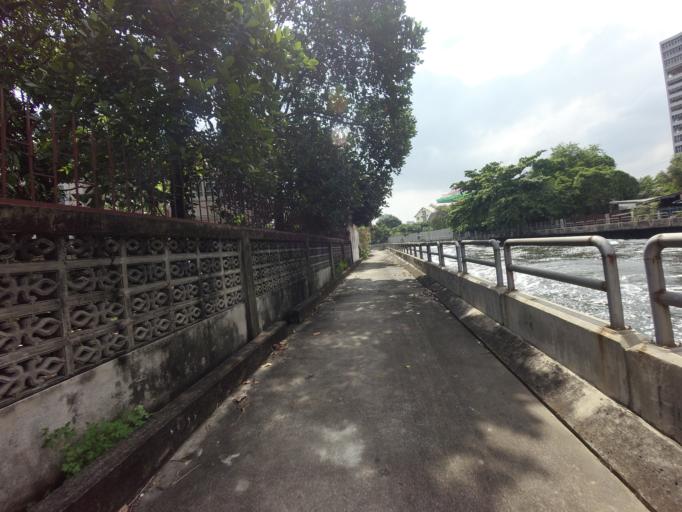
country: TH
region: Bangkok
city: Watthana
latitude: 13.7477
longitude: 100.6008
